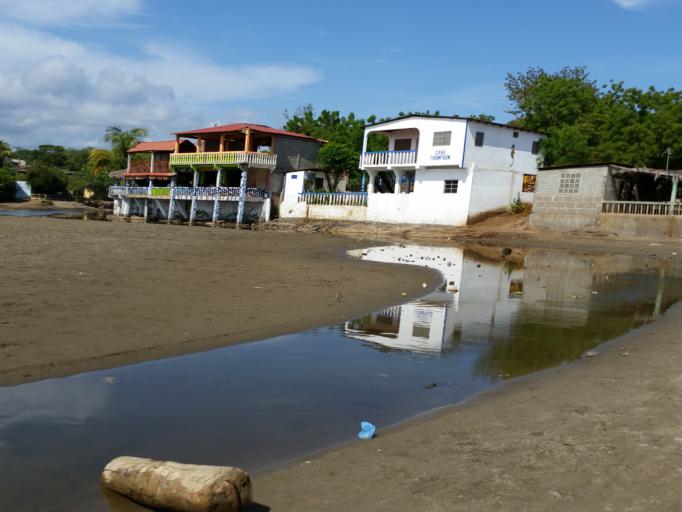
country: NI
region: Managua
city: Masachapa
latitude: 11.7826
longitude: -86.5174
